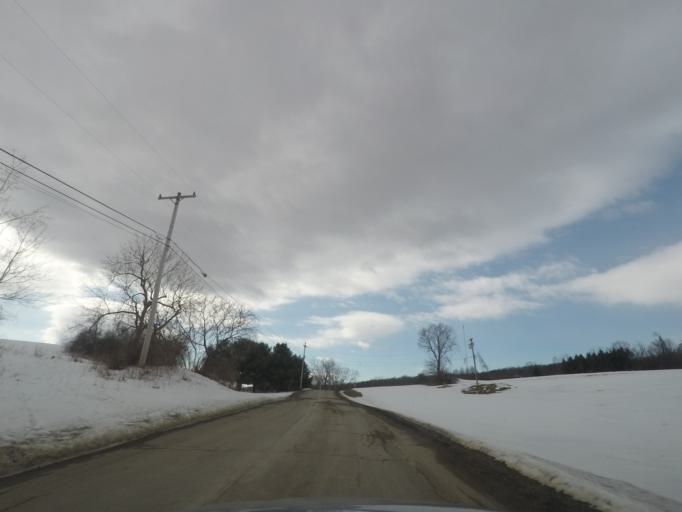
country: US
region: New York
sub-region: Saratoga County
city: Waterford
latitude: 42.7823
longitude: -73.6142
